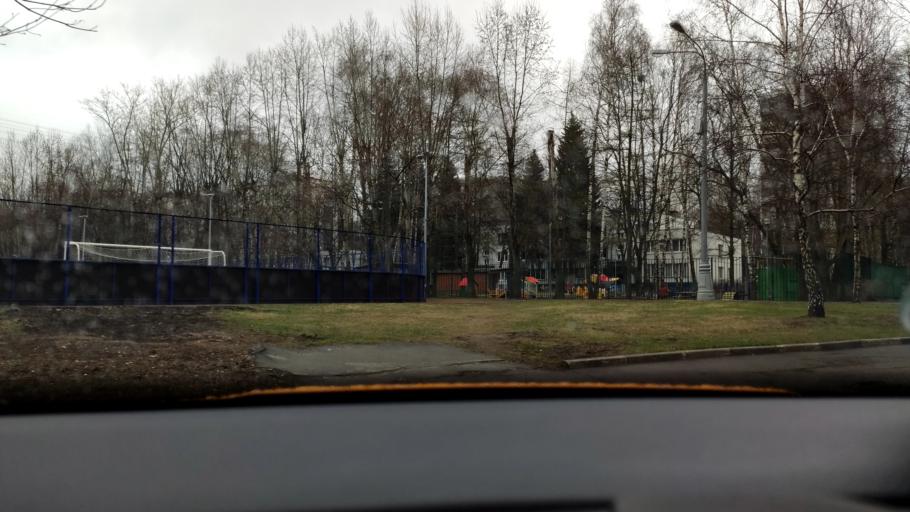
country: RU
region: Moscow
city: Troparevo
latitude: 55.6470
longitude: 37.5195
